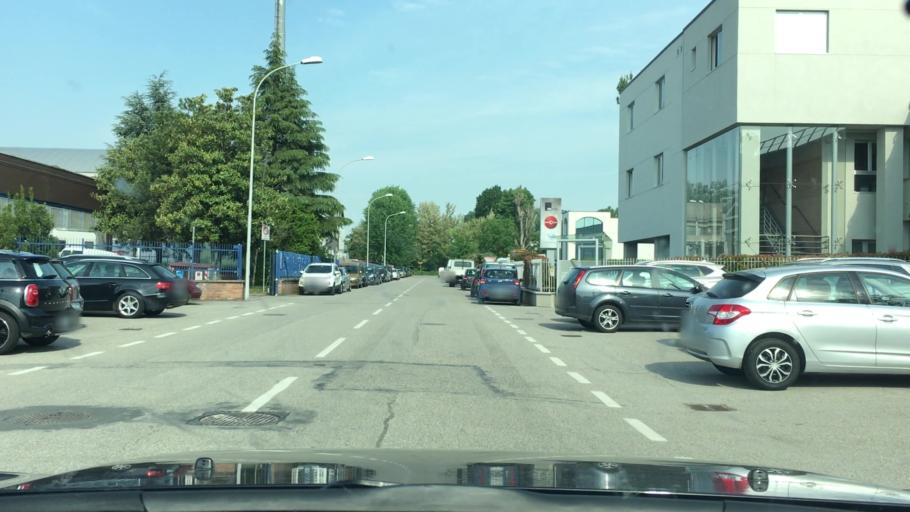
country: IT
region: Emilia-Romagna
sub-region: Provincia di Bologna
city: Quarto Inferiore
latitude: 44.5514
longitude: 11.3933
